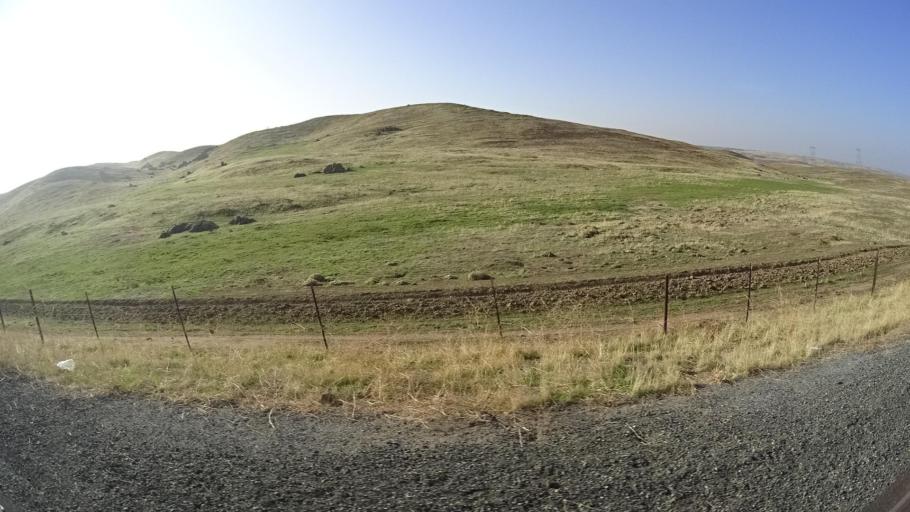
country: US
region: California
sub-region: Tulare County
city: Richgrove
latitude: 35.7419
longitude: -118.9136
